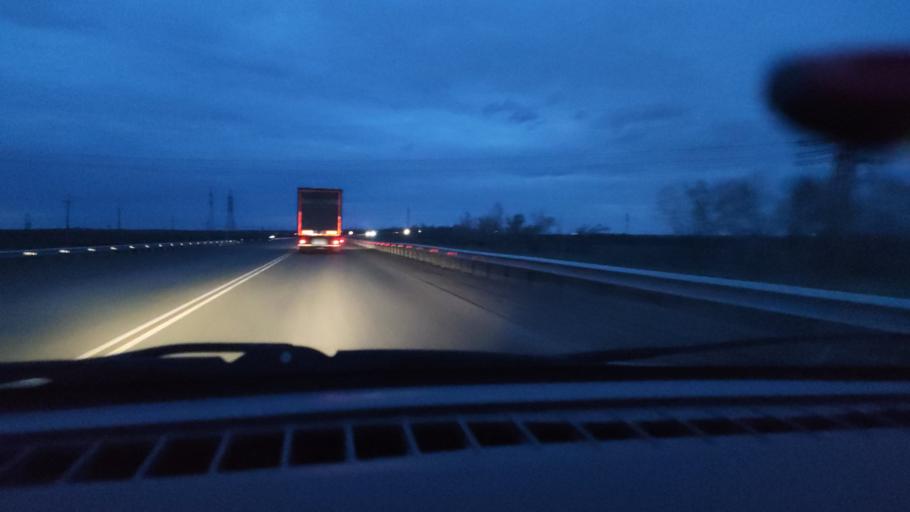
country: RU
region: Orenburg
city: Tatarskaya Kargala
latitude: 51.9798
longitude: 55.1875
